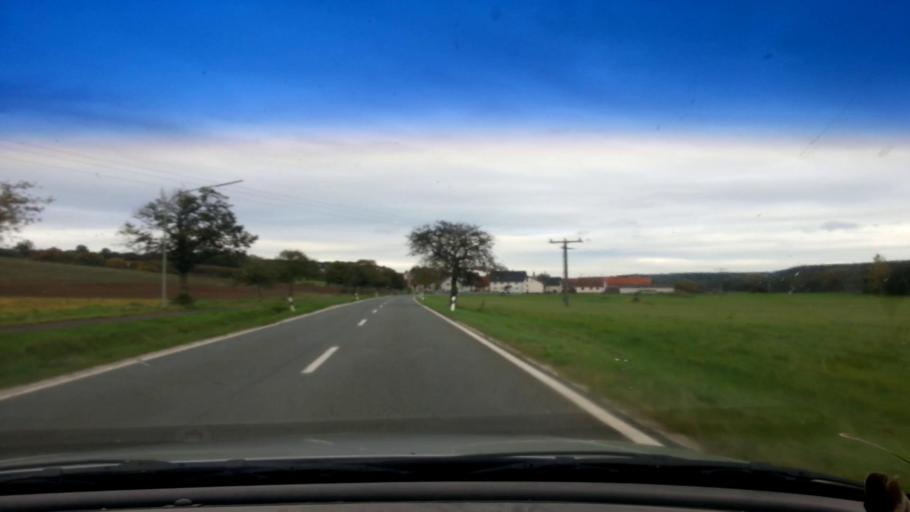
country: DE
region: Bavaria
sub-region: Upper Franconia
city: Burgwindheim
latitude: 49.8718
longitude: 10.6317
